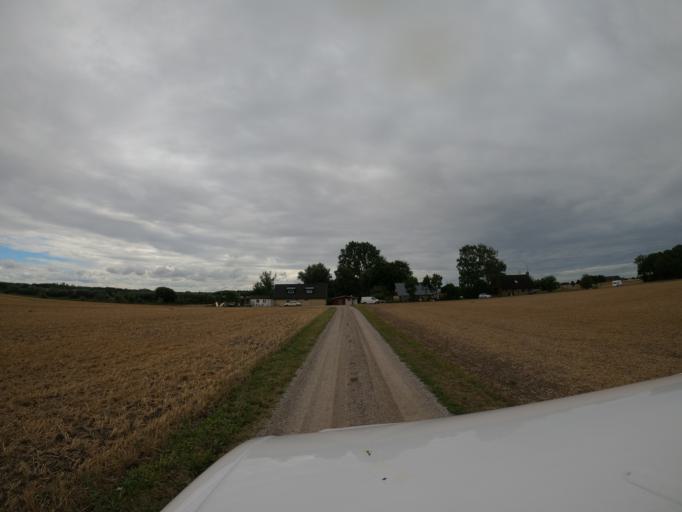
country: SE
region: Skane
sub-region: Lunds Kommun
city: Lund
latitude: 55.7397
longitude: 13.1498
